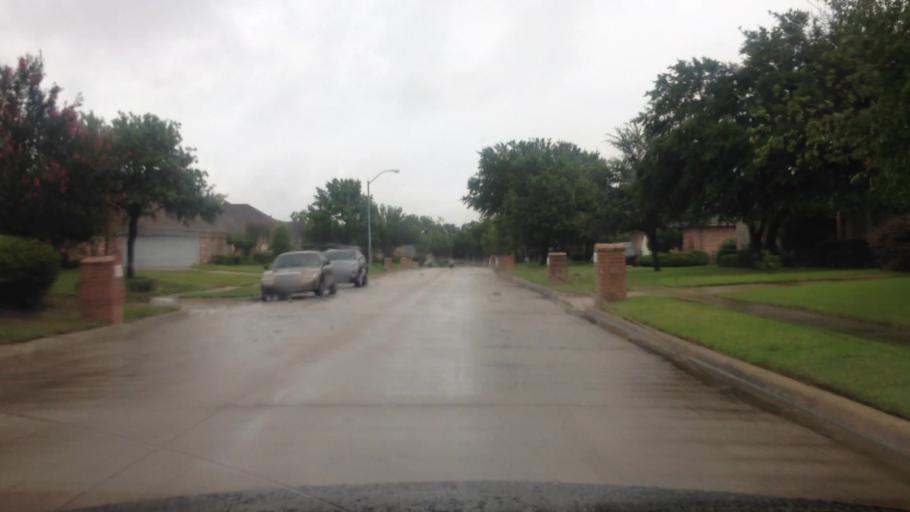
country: US
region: Texas
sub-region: Tarrant County
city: Colleyville
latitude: 32.9018
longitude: -97.2061
